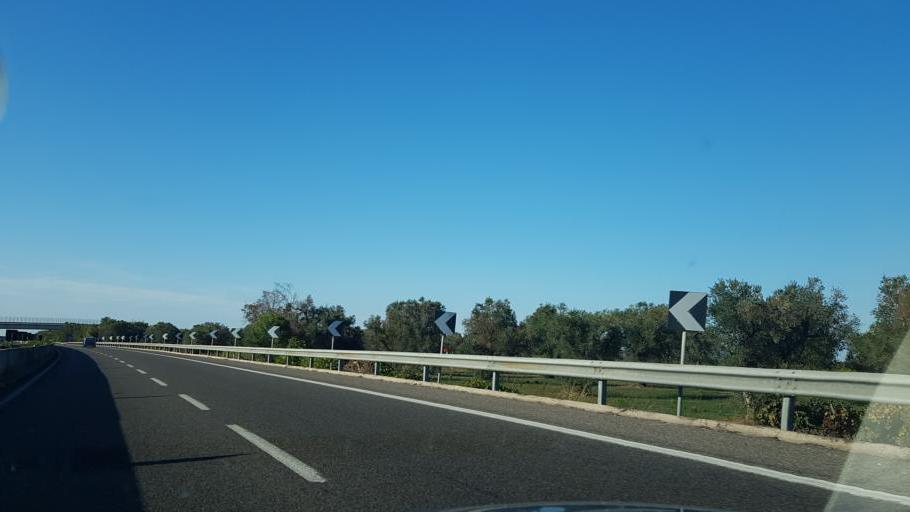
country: IT
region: Apulia
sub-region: Provincia di Brindisi
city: San Pietro Vernotico
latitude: 40.5325
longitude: 18.0096
